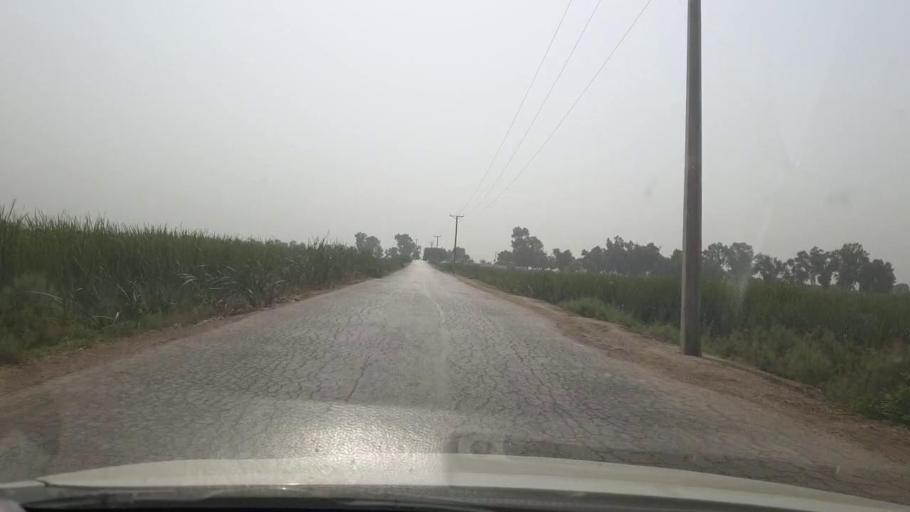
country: PK
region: Sindh
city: Kot Diji
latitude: 27.4351
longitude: 68.6460
